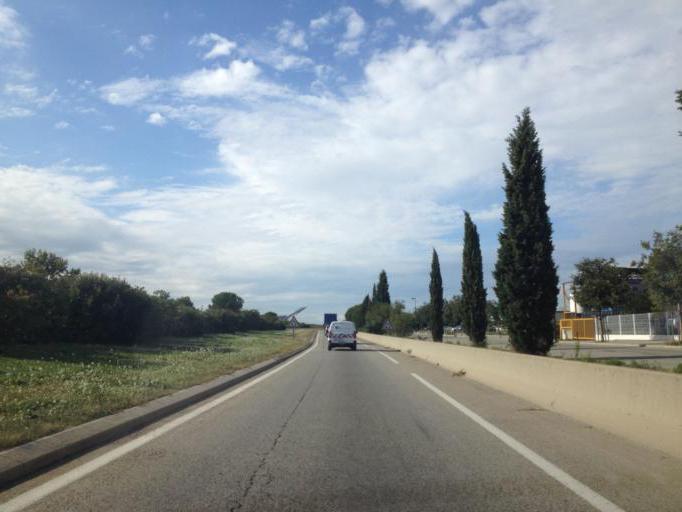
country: FR
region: Provence-Alpes-Cote d'Azur
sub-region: Departement du Vaucluse
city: Courthezon
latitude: 44.1102
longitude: 4.8494
